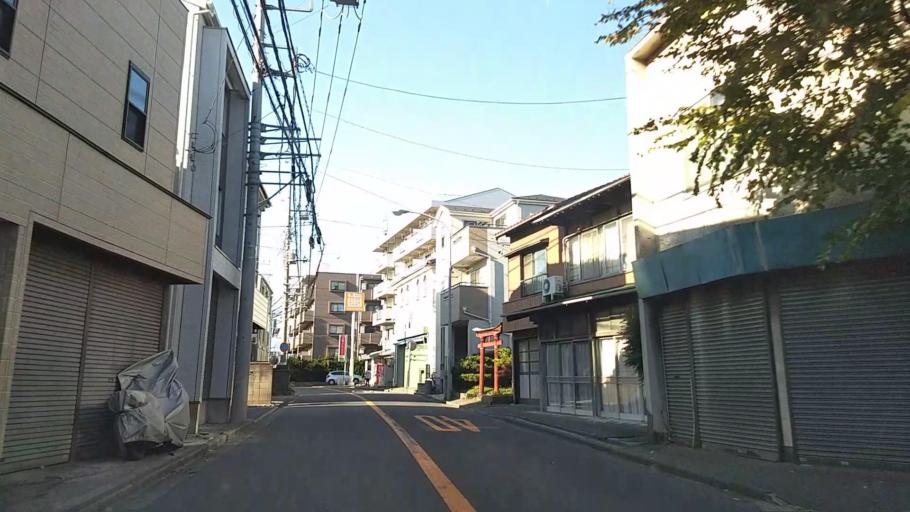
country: JP
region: Tokyo
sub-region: Machida-shi
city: Machida
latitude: 35.5256
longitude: 139.5507
